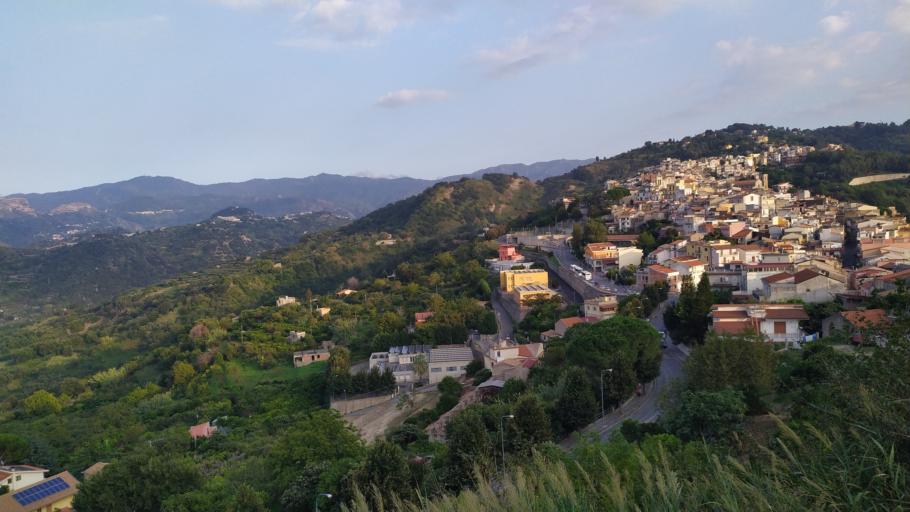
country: IT
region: Sicily
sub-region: Messina
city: San Pier Niceto
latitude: 38.1621
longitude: 15.3474
